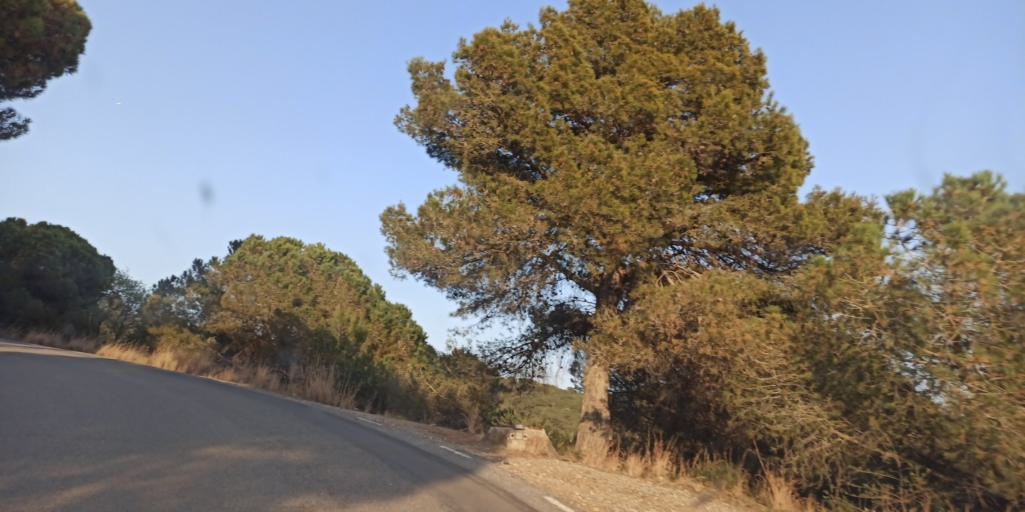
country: ES
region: Catalonia
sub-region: Provincia de Barcelona
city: Sant Just Desvern
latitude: 41.4059
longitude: 2.0861
